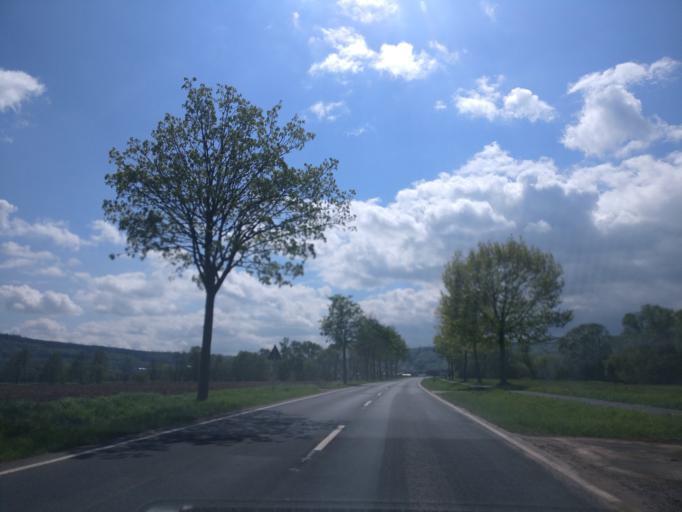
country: DE
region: Lower Saxony
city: Hannoversch Munden
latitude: 51.4493
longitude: 9.6448
